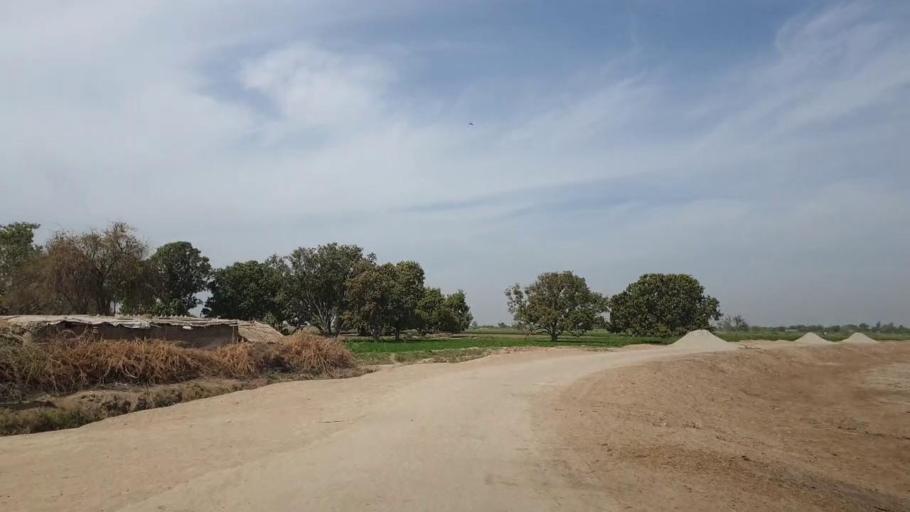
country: PK
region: Sindh
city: Kunri
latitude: 25.2127
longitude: 69.5742
